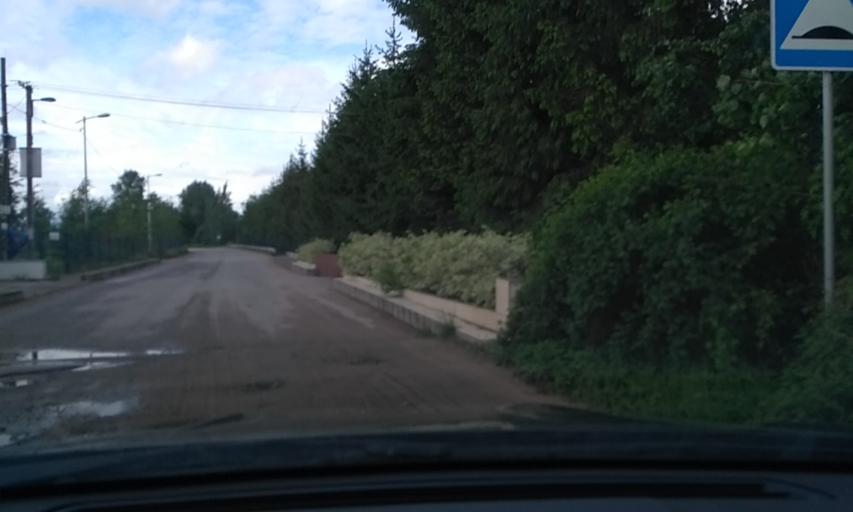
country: RU
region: Leningrad
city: Otradnoye
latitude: 59.7942
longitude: 30.7970
